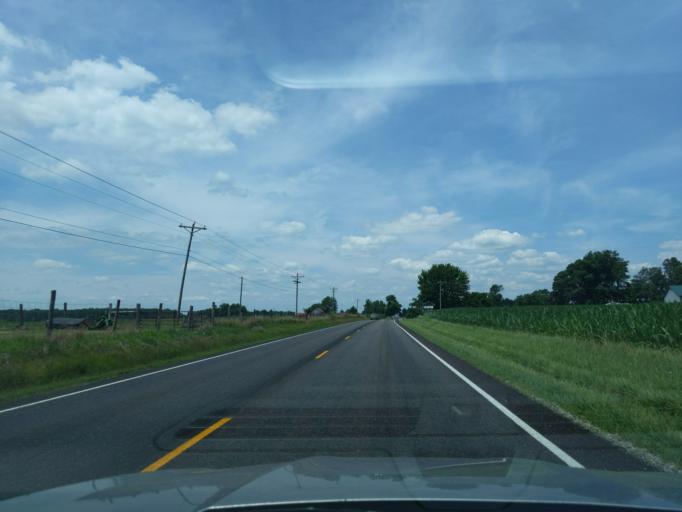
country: US
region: Indiana
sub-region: Ripley County
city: Osgood
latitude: 39.2109
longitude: -85.3318
